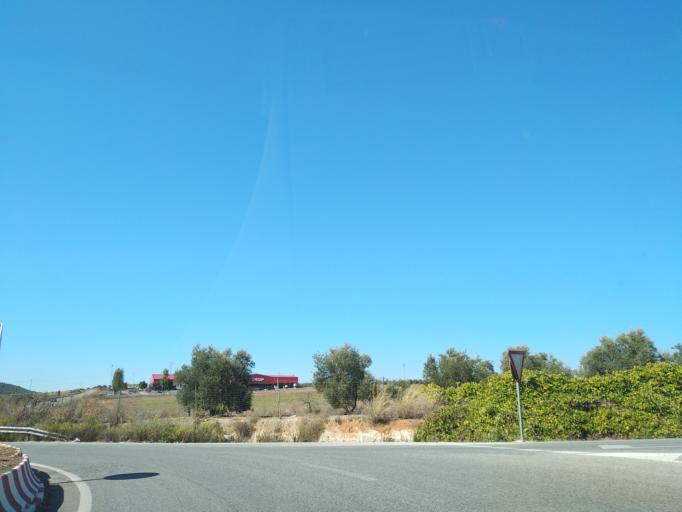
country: ES
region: Andalusia
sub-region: Provincia de Malaga
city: Mollina
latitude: 37.1182
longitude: -4.6691
